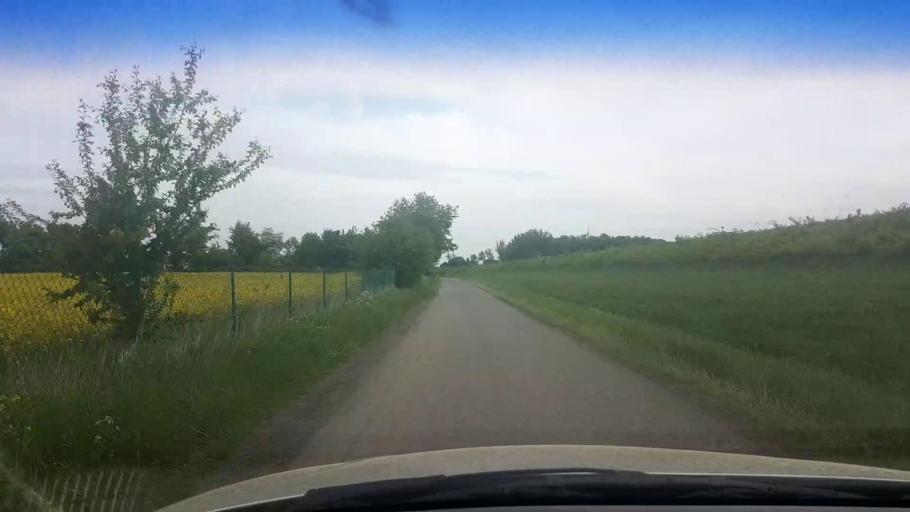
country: DE
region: Bavaria
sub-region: Upper Franconia
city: Bamberg
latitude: 49.8738
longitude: 10.9129
